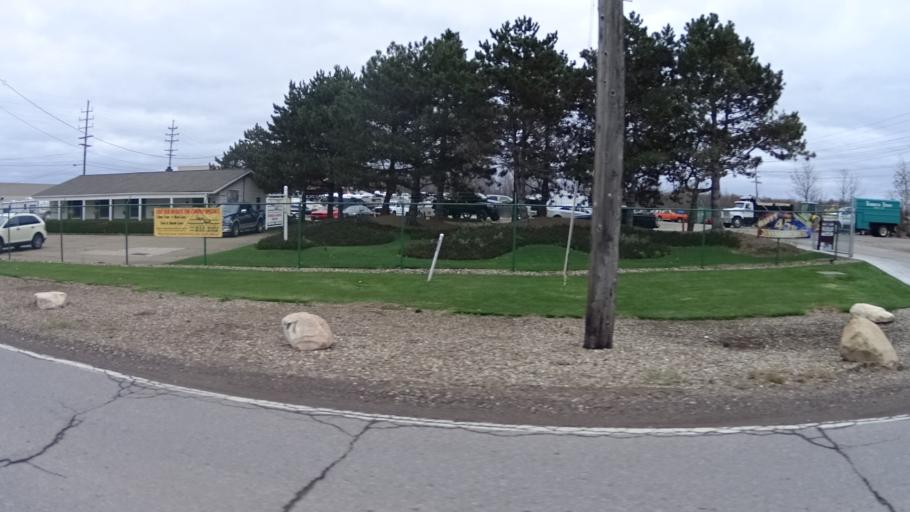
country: US
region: Ohio
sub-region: Lorain County
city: Avon
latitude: 41.4791
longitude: -82.0472
